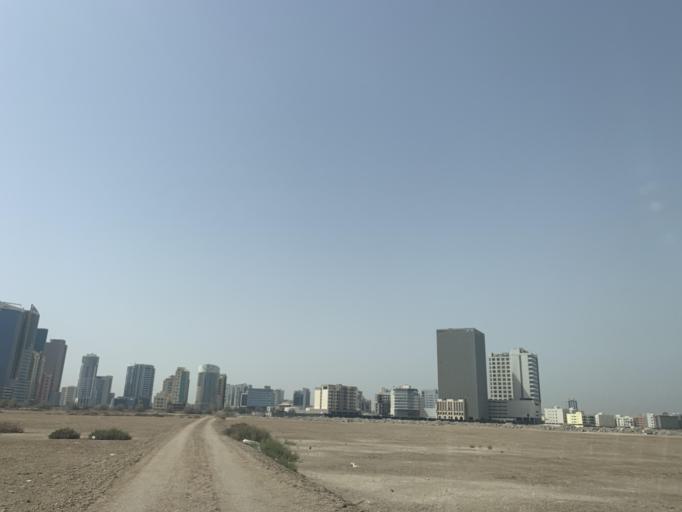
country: BH
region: Manama
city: Jidd Hafs
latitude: 26.2469
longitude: 50.5331
